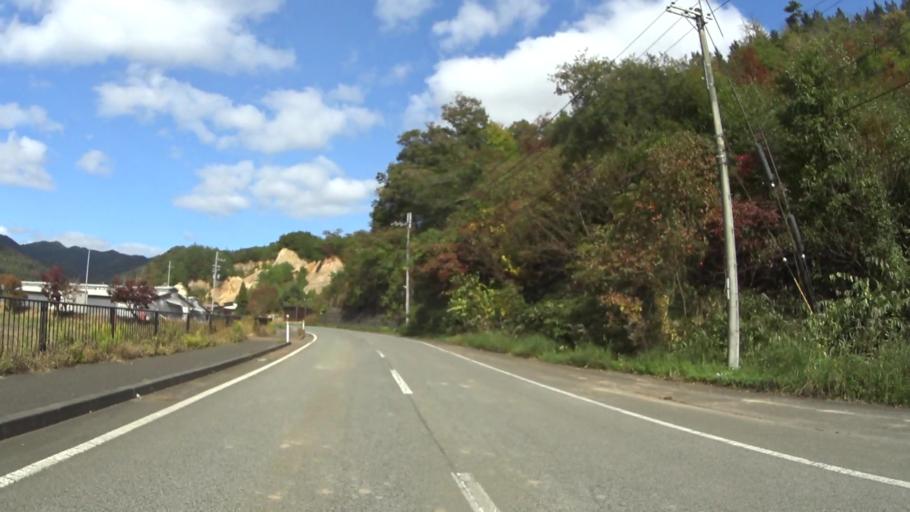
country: JP
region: Hyogo
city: Toyooka
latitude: 35.5017
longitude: 134.9926
